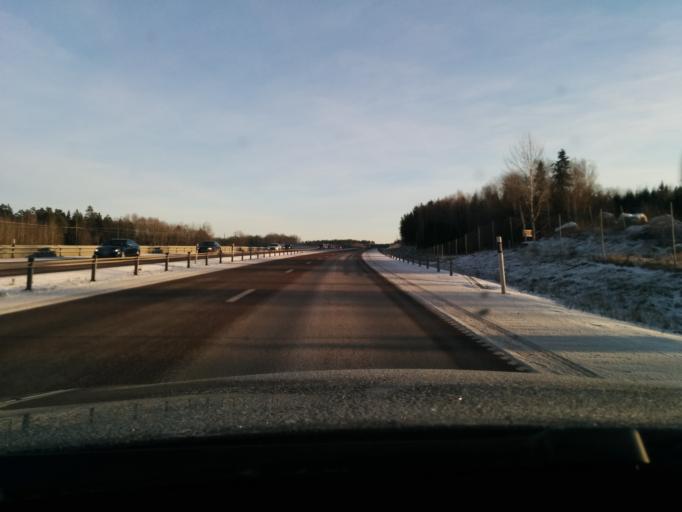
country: SE
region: Uppsala
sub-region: Enkopings Kommun
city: Hummelsta
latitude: 59.6490
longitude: 16.9896
